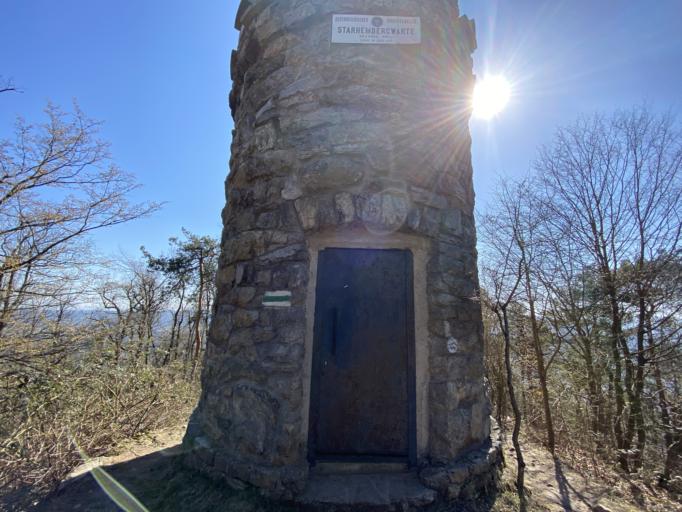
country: AT
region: Lower Austria
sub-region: Politischer Bezirk Krems
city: Durnstein
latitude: 48.4050
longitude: 15.5302
